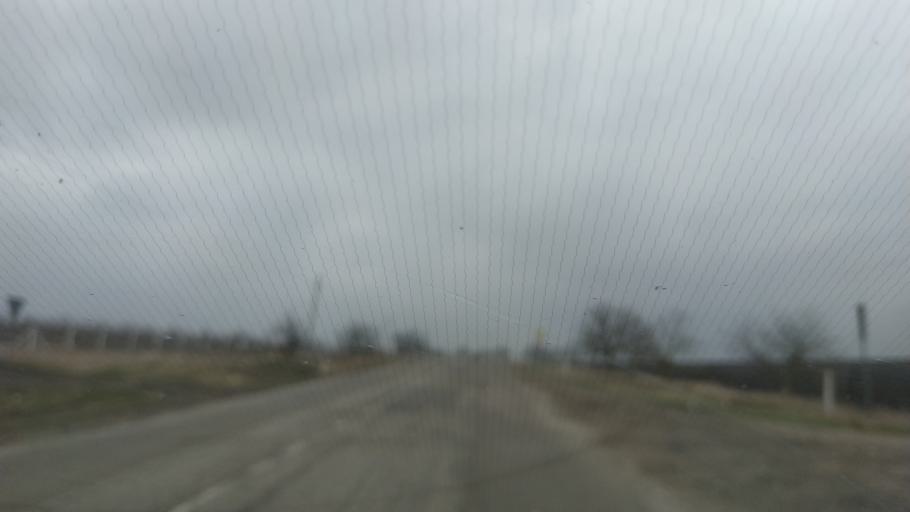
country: MD
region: Gagauzia
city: Comrat
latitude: 46.2694
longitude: 28.7321
